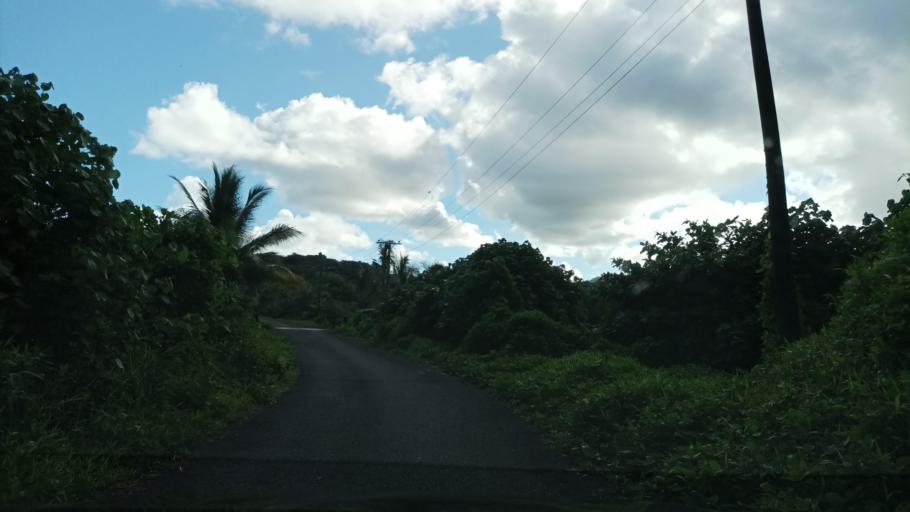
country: FM
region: Pohnpei
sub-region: Madolenihm Municipality
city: Madolenihm Municipality Government
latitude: 6.8457
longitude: 158.3153
